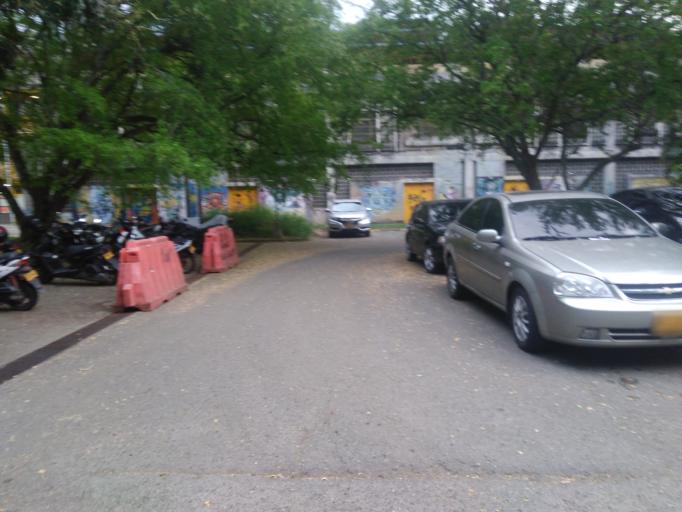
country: CO
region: Valle del Cauca
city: Cali
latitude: 3.3763
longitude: -76.5353
